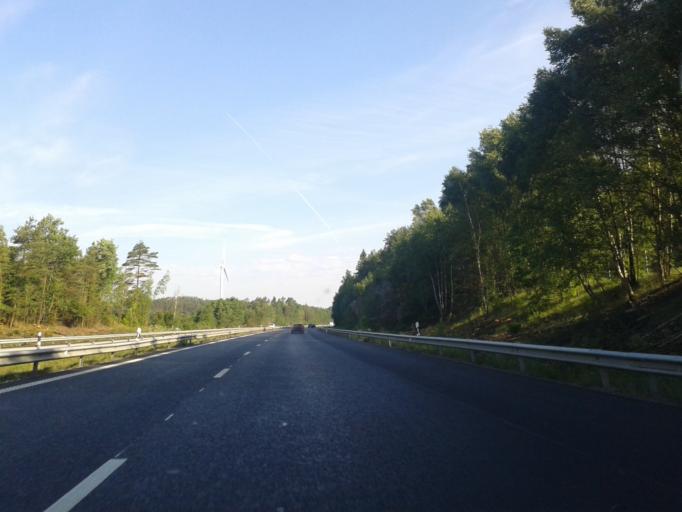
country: SE
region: Vaestra Goetaland
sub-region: Kungalvs Kommun
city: Kode
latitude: 57.9158
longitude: 11.8870
